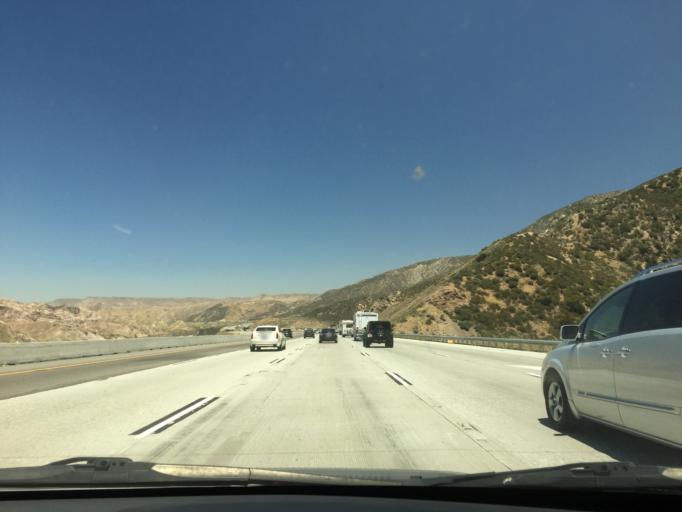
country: US
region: California
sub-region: San Bernardino County
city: Oak Hills
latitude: 34.2662
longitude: -117.4494
